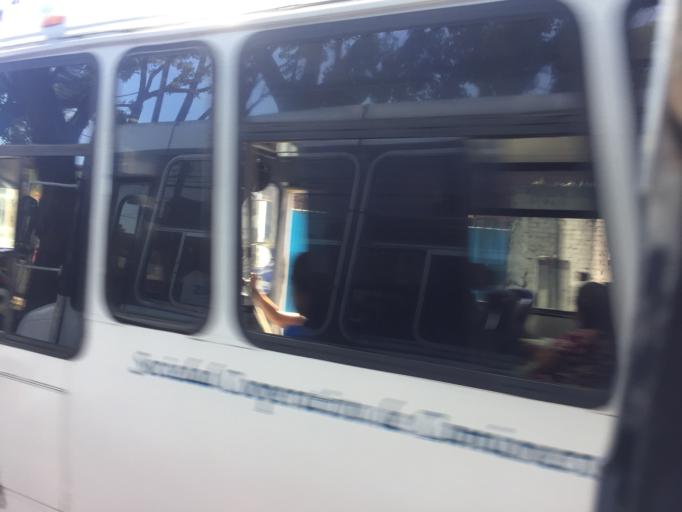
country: MX
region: Veracruz
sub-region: Xalapa
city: Xalapa de Enriquez
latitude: 19.5333
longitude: -96.9082
